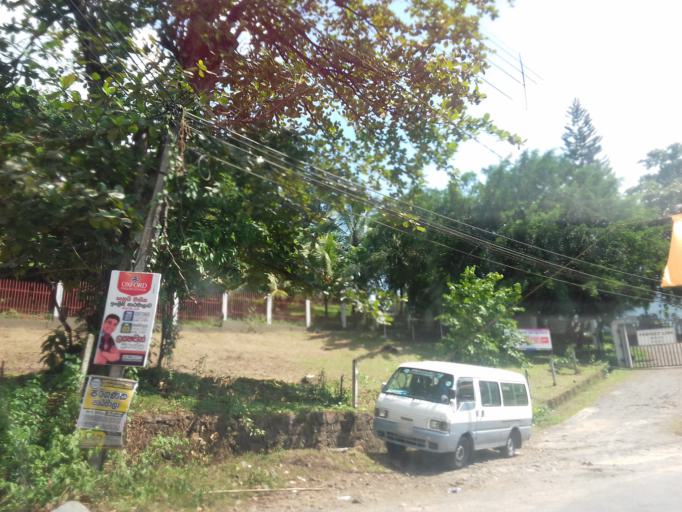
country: LK
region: Central
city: Hatton
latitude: 6.9976
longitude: 80.3593
